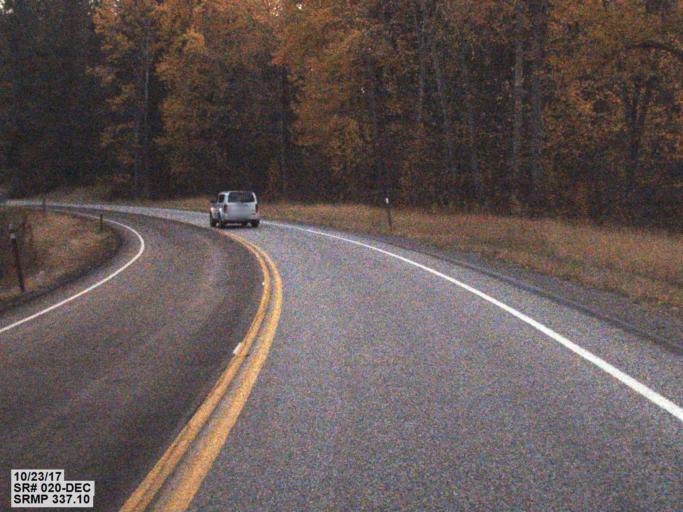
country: US
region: Washington
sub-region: Stevens County
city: Kettle Falls
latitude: 48.5919
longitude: -118.1868
